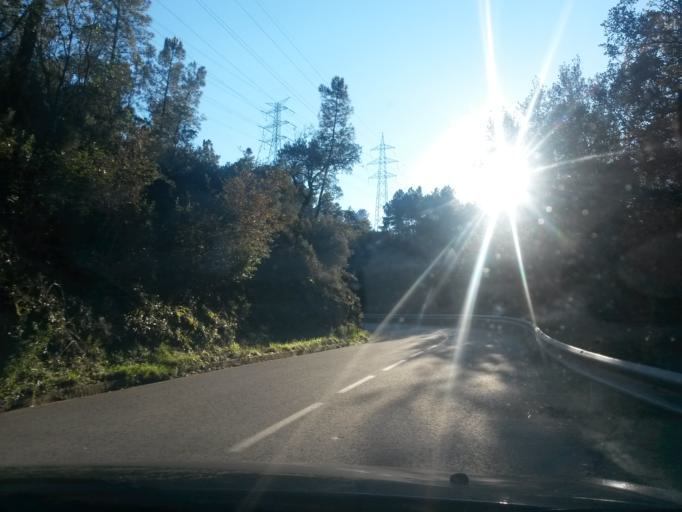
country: ES
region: Catalonia
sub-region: Provincia de Girona
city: Angles
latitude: 41.9533
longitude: 2.6753
